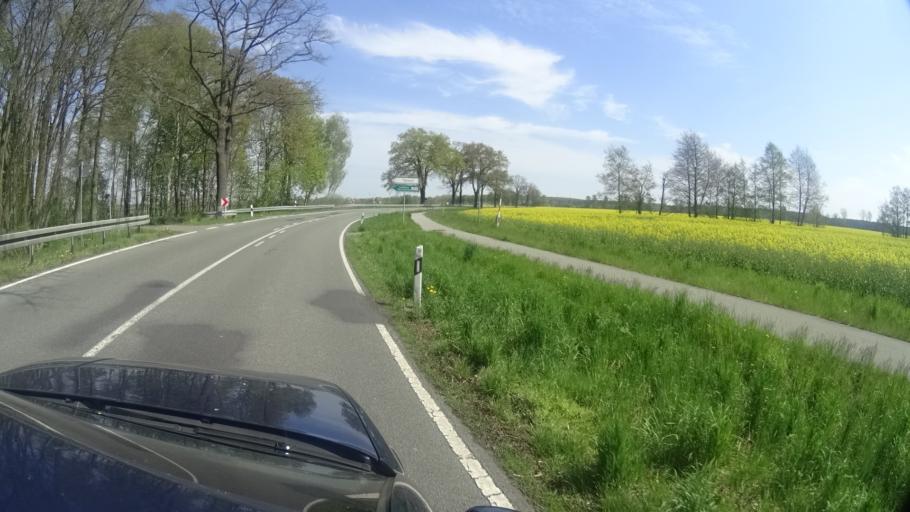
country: DE
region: Brandenburg
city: Dreetz
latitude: 52.8332
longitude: 12.4302
